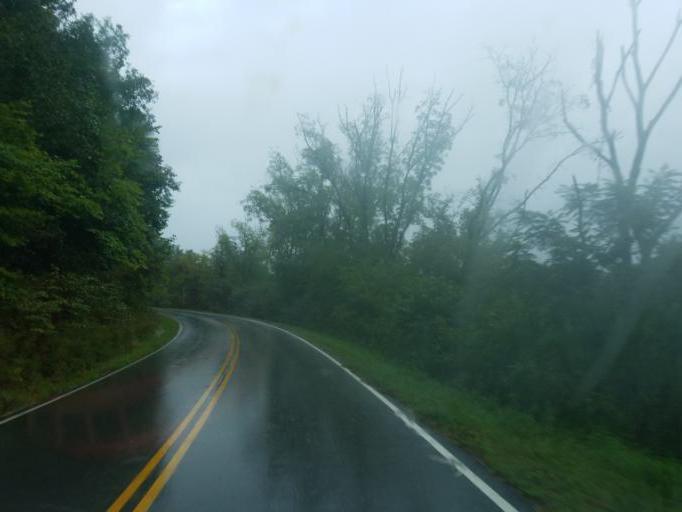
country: US
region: Kentucky
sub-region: Carter County
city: Grayson
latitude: 38.4683
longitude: -83.0468
